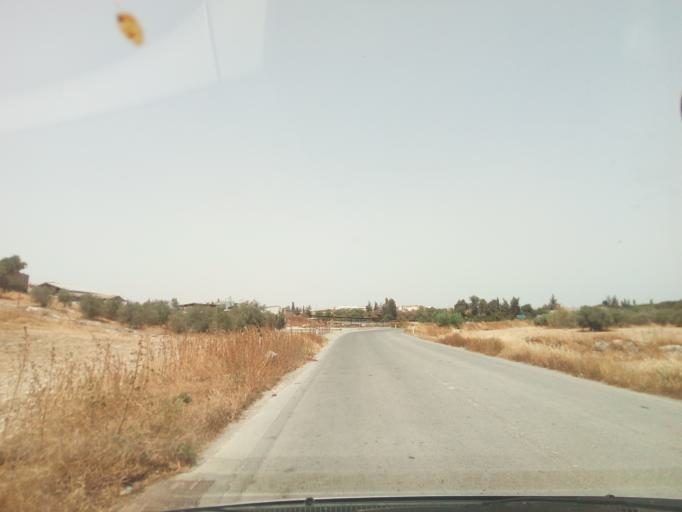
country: CY
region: Larnaka
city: Aradippou
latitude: 34.9588
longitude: 33.5852
